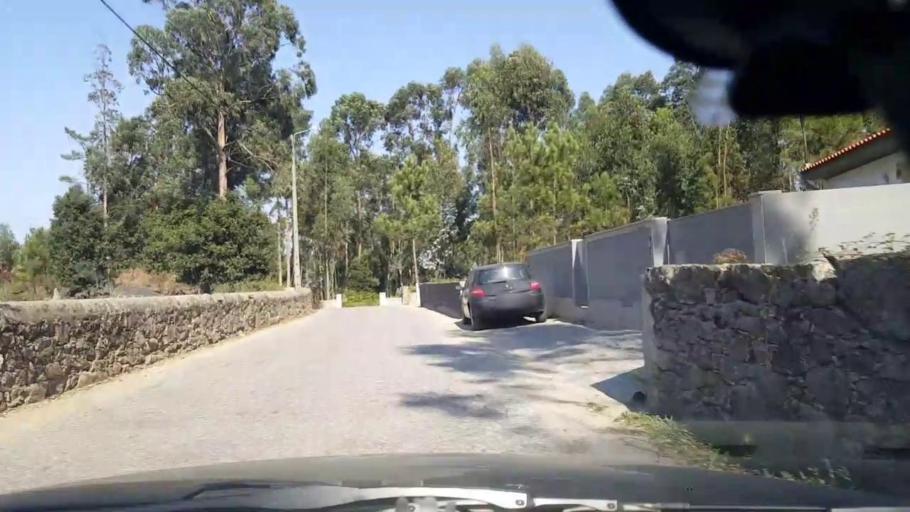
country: PT
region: Porto
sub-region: Povoa de Varzim
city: Pedroso
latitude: 41.4084
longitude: -8.7067
